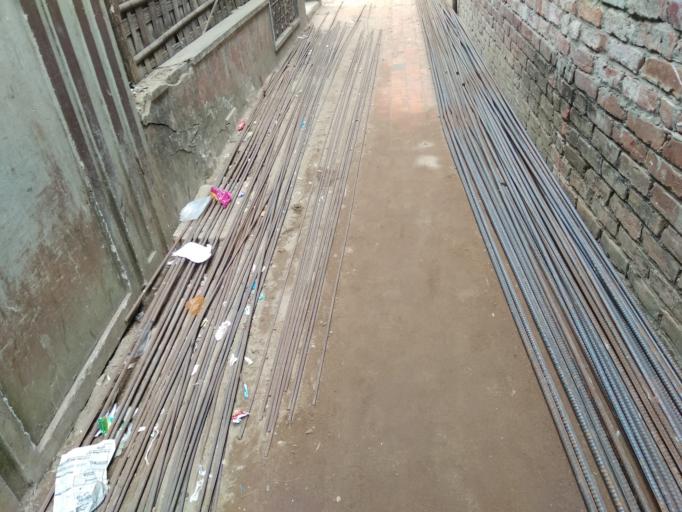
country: BD
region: Chittagong
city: Chittagong
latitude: 22.3708
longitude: 91.8366
